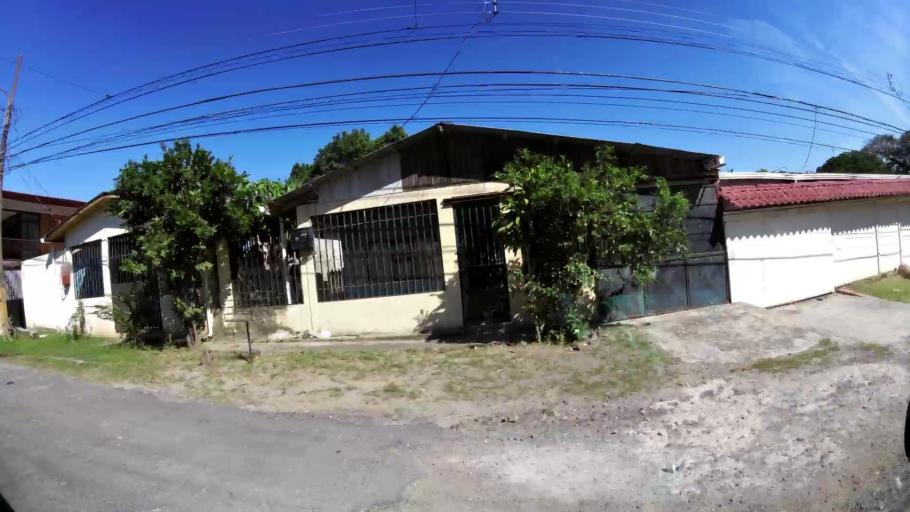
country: CR
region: Guanacaste
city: Liberia
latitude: 10.6319
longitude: -85.4326
